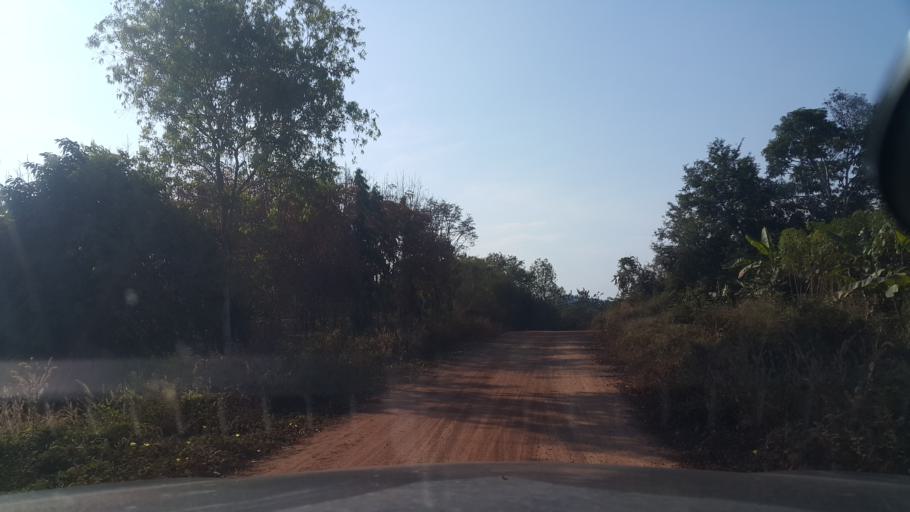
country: TH
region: Loei
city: Chiang Khan
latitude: 17.8230
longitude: 101.6171
